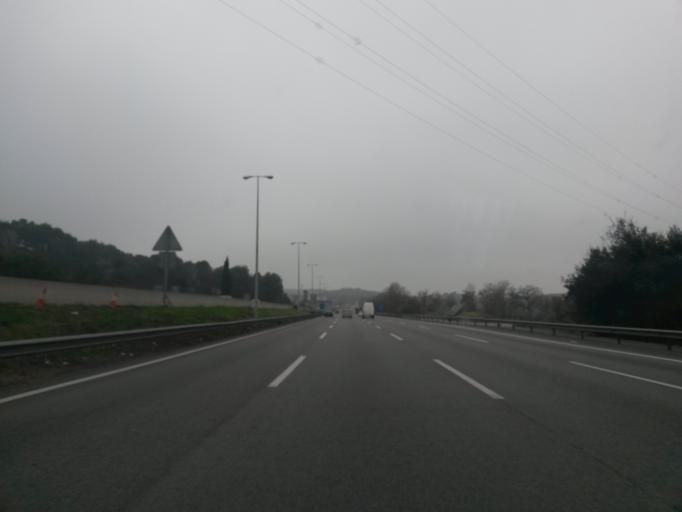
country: ES
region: Catalonia
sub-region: Provincia de Barcelona
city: Granollers
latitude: 41.5895
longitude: 2.3055
